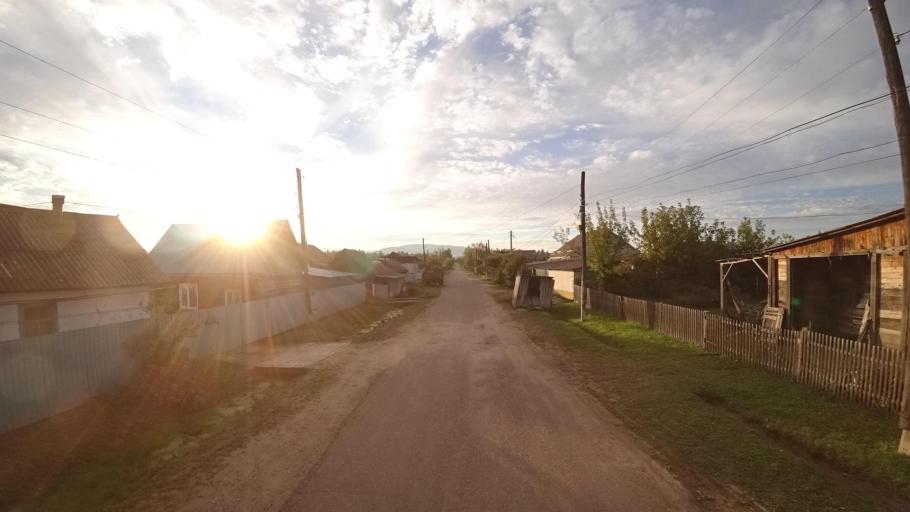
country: RU
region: Primorskiy
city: Yakovlevka
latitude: 44.4249
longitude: 133.4863
